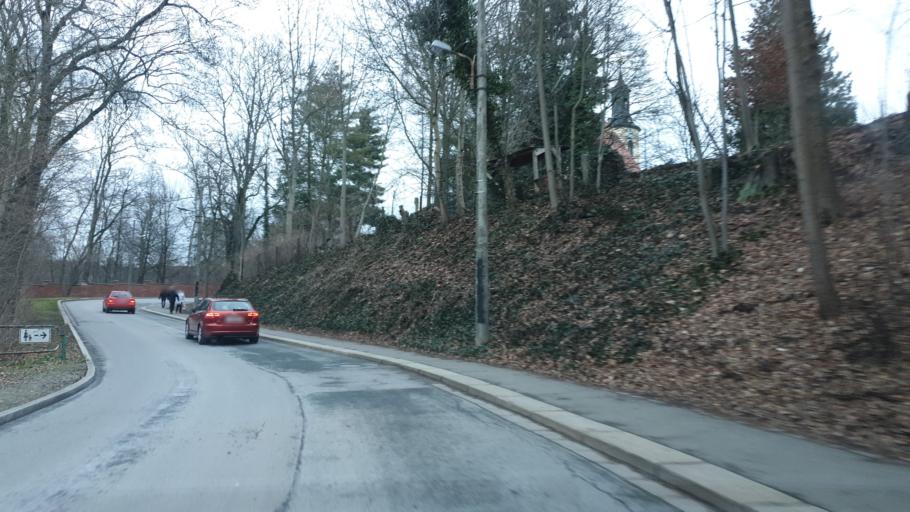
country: DE
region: Saxony
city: Lichtenstein
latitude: 50.7537
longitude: 12.6279
